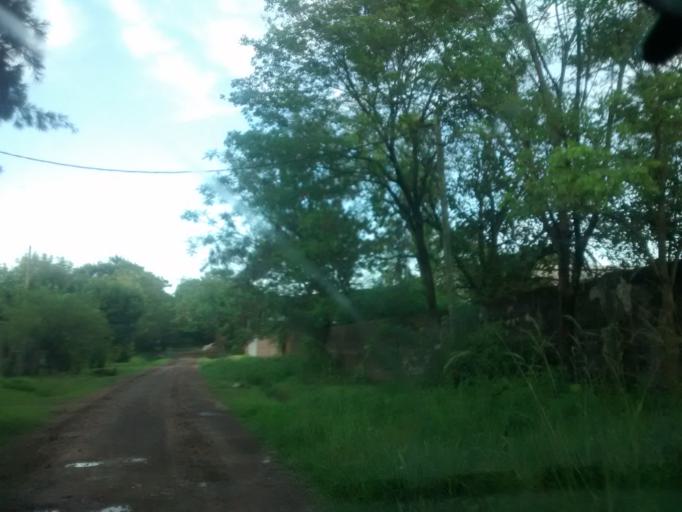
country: AR
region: Chaco
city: Fontana
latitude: -27.4198
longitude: -59.0043
